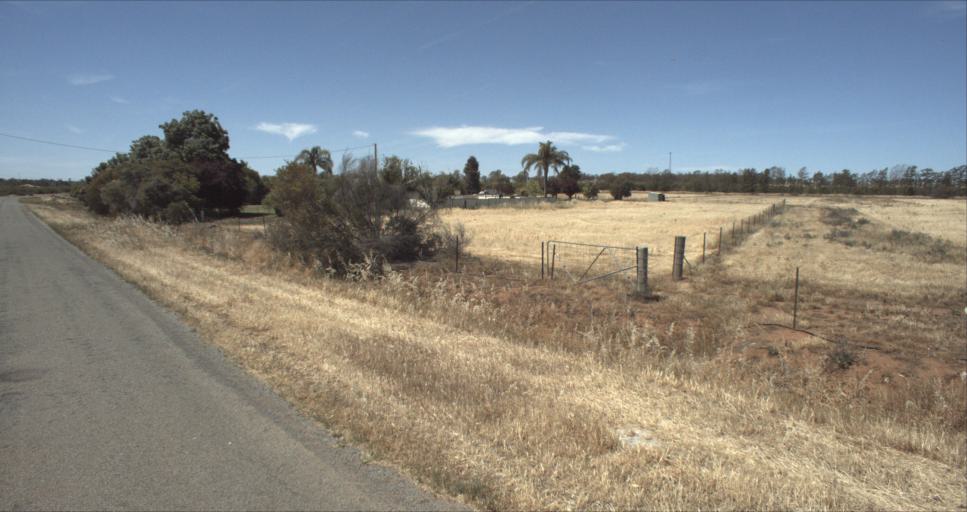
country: AU
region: New South Wales
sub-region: Leeton
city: Leeton
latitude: -34.5983
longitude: 146.4368
